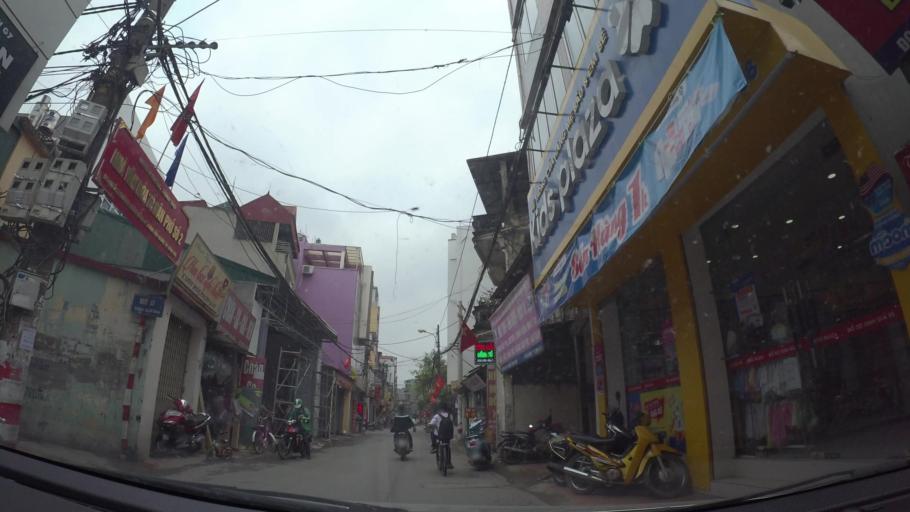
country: VN
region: Ha Noi
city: Tay Ho
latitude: 21.0695
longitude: 105.8021
